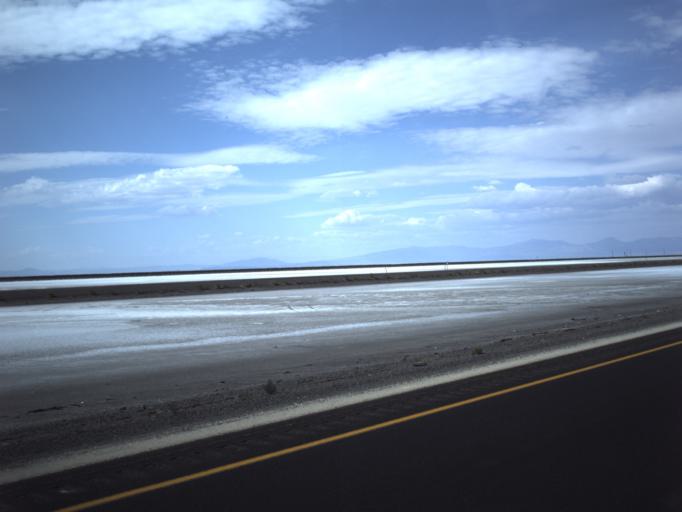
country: US
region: Utah
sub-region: Tooele County
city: Wendover
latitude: 40.7342
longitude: -113.6054
